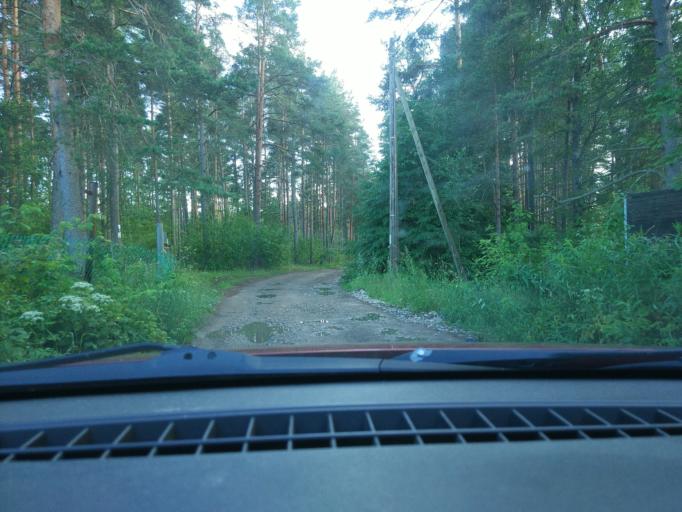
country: RU
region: Leningrad
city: Priozersk
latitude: 60.9420
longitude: 30.0465
